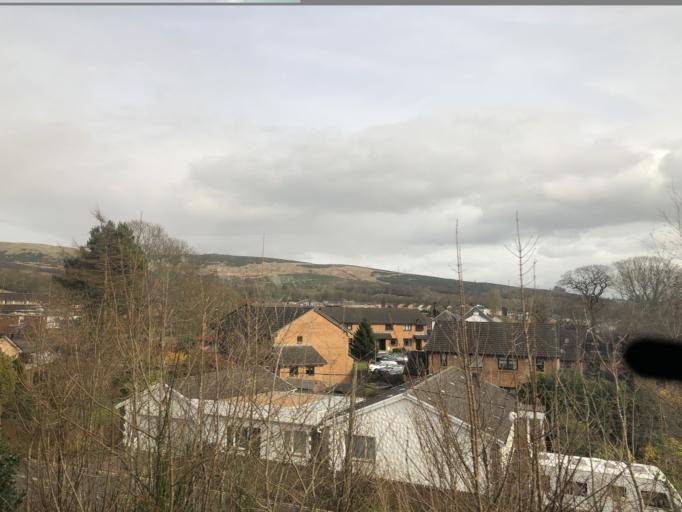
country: GB
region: Scotland
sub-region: Argyll and Bute
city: Helensburgh
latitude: 56.0003
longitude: -4.7119
